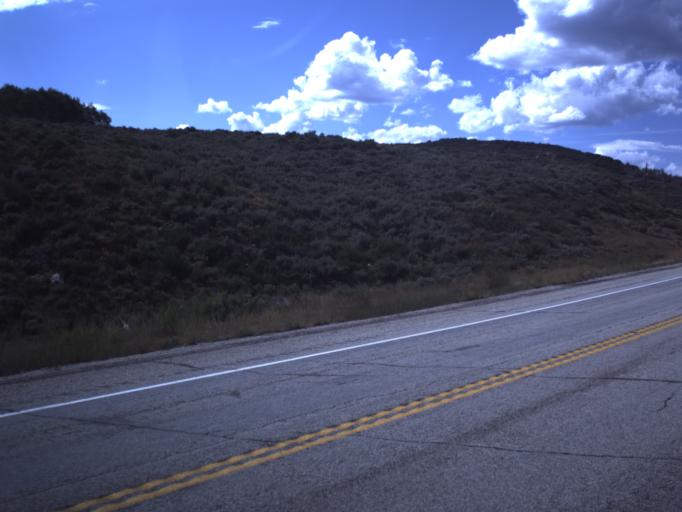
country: US
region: Utah
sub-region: Summit County
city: Francis
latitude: 40.2023
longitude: -110.9695
